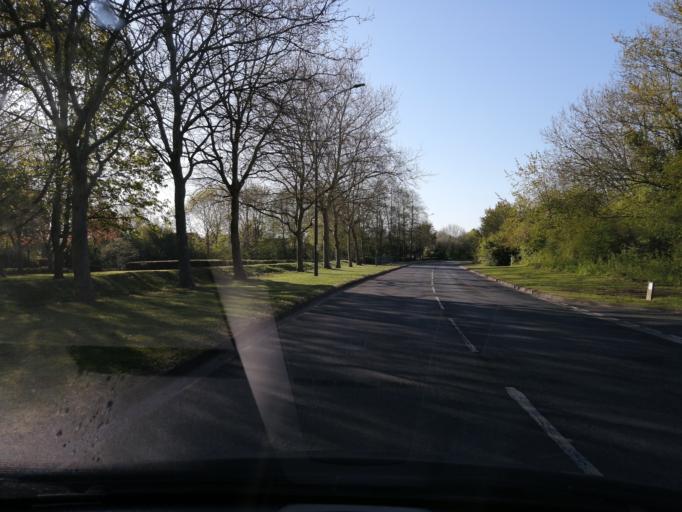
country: GB
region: England
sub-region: Peterborough
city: Castor
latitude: 52.5569
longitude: -0.3071
